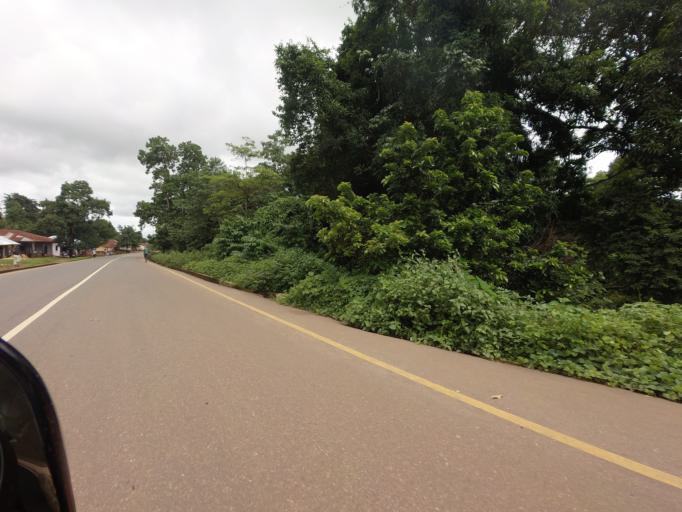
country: SL
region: Northern Province
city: Kambia
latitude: 9.1268
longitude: -12.9107
